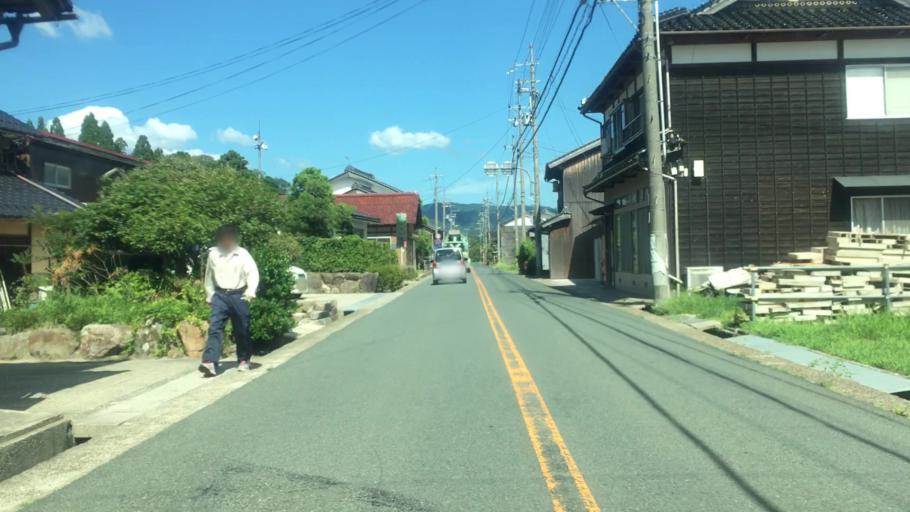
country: JP
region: Kyoto
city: Miyazu
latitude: 35.6083
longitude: 135.0494
